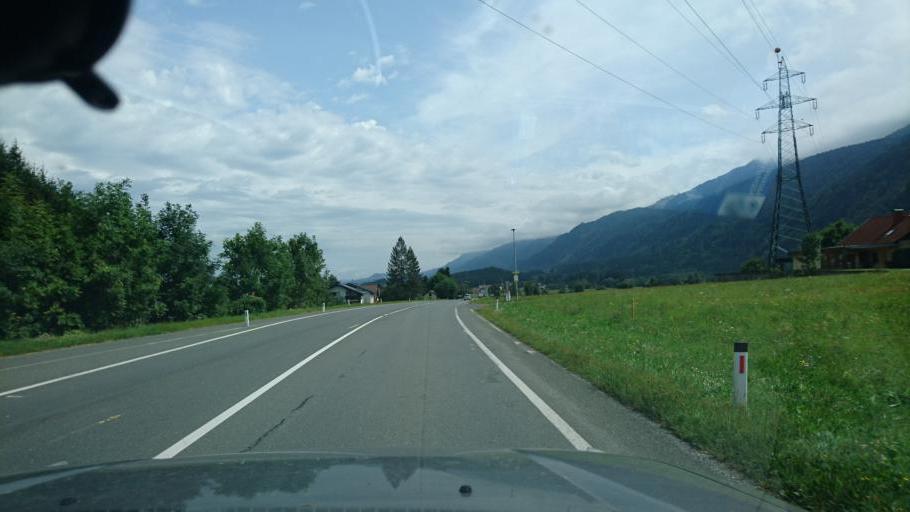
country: AT
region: Carinthia
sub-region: Politischer Bezirk Villach Land
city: Arnoldstein
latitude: 46.5480
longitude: 13.7387
